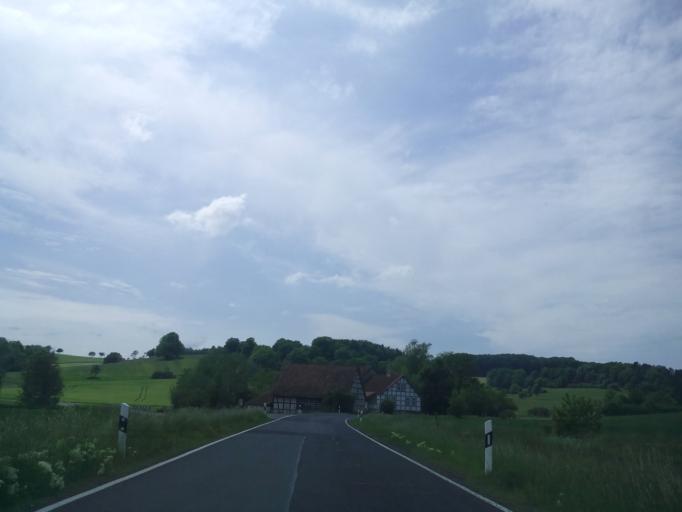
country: DE
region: Bavaria
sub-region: Upper Franconia
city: Weitramsdorf
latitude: 50.2640
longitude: 10.8080
